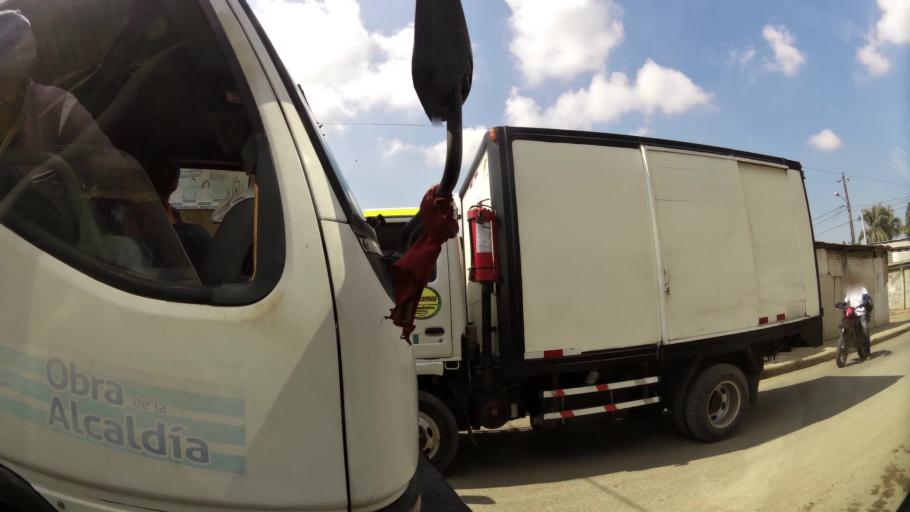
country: EC
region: Guayas
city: Eloy Alfaro
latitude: -2.1658
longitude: -79.8241
